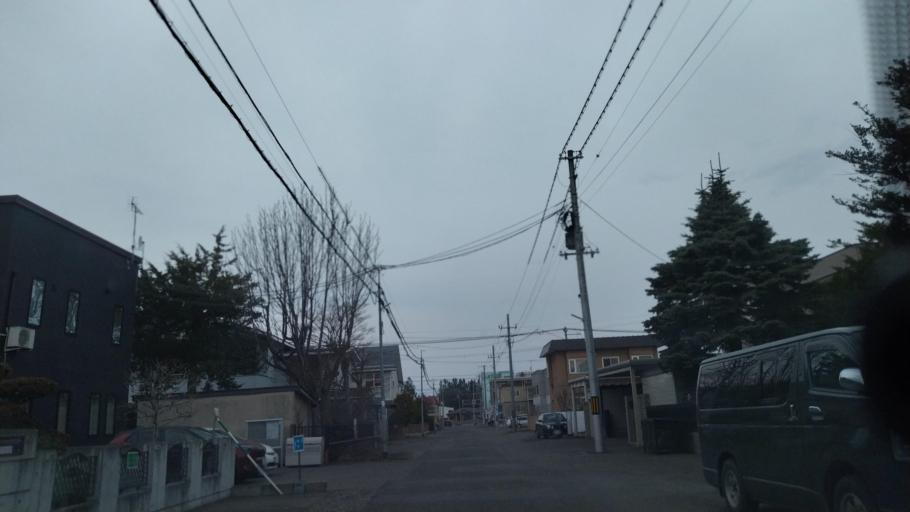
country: JP
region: Hokkaido
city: Obihiro
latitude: 42.9247
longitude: 143.2106
